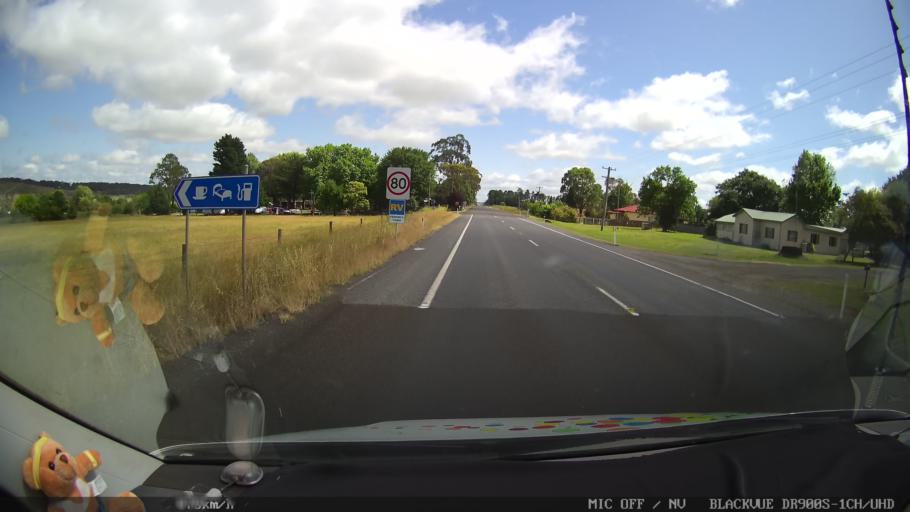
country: AU
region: New South Wales
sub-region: Glen Innes Severn
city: Glen Innes
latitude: -29.7727
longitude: 151.7317
